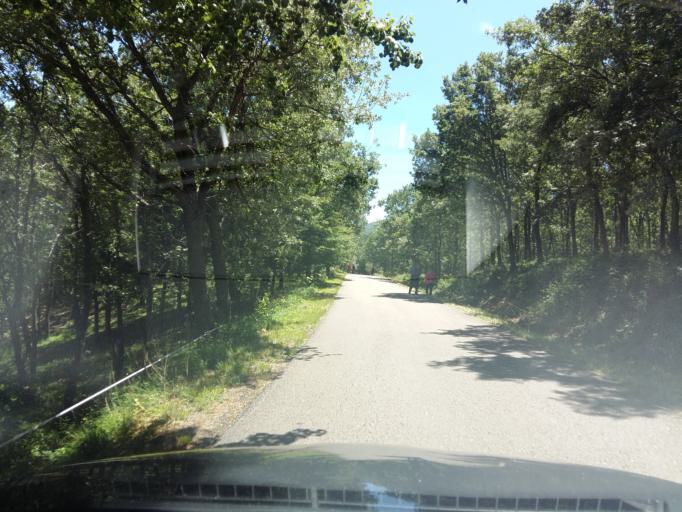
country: ES
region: Castille and Leon
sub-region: Provincia de Soria
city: Vozmediano
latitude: 41.8131
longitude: -1.8168
